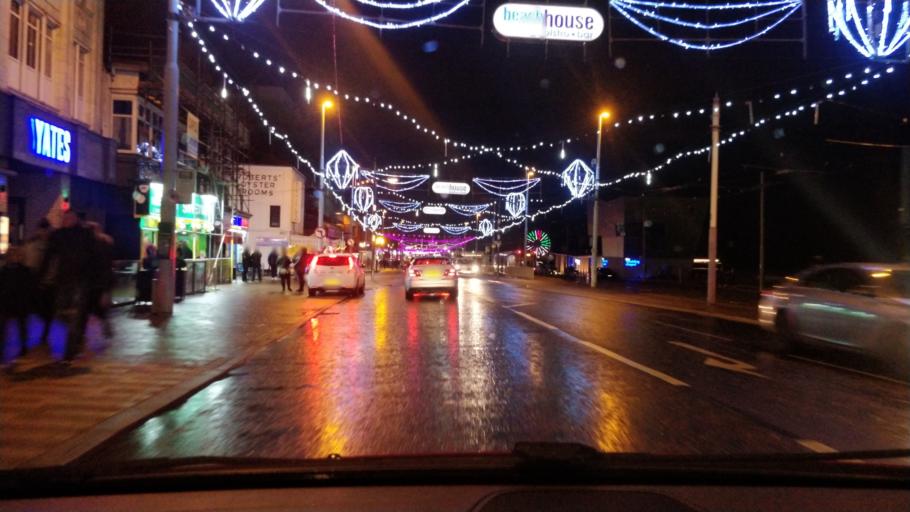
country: GB
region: England
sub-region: Blackpool
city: Blackpool
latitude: 53.8186
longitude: -3.0559
